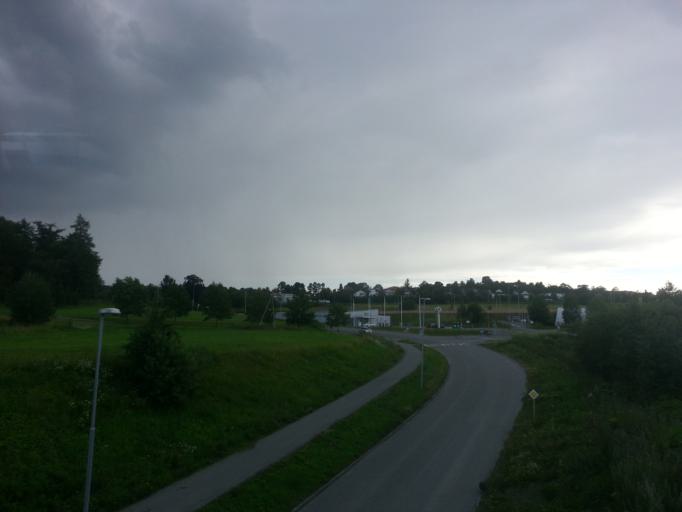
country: NO
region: Sor-Trondelag
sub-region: Trondheim
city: Trondheim
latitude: 63.4329
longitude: 10.4979
